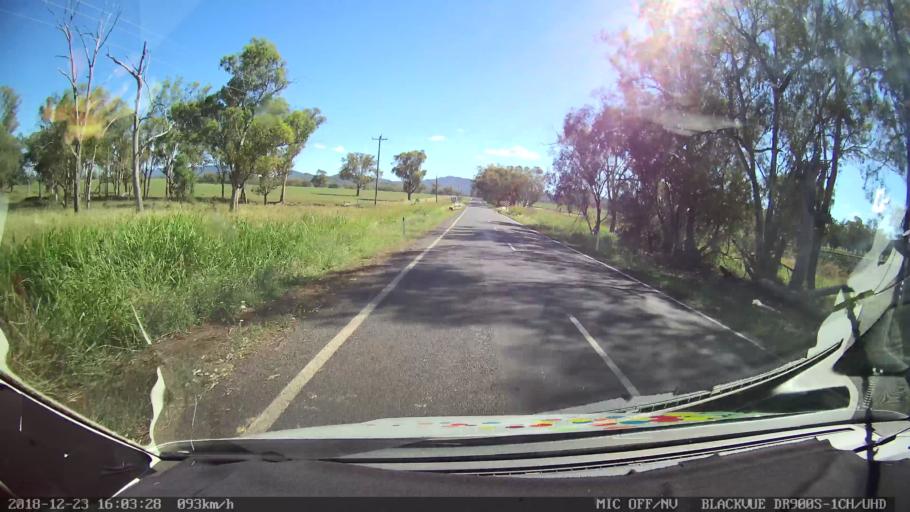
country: AU
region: New South Wales
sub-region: Tamworth Municipality
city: Phillip
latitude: -31.2439
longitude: 150.8005
